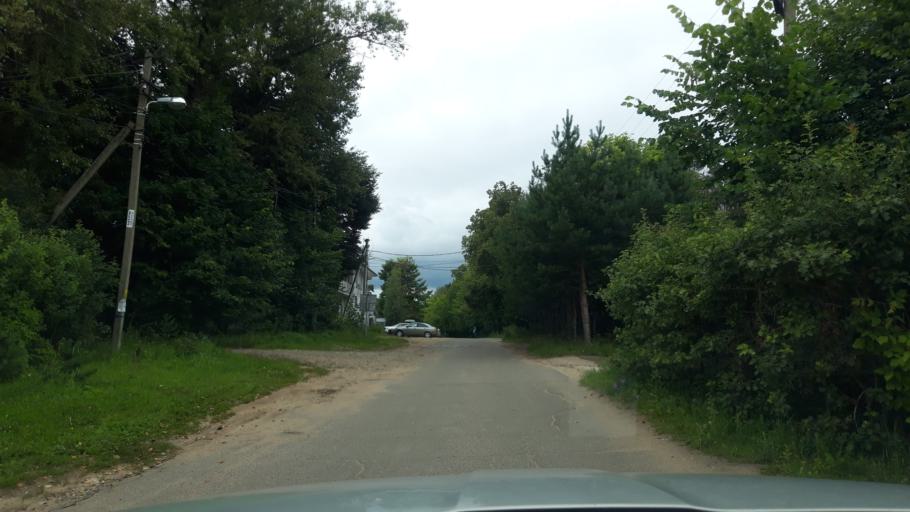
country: RU
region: Moskovskaya
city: Povarovo
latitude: 56.0602
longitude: 37.0591
